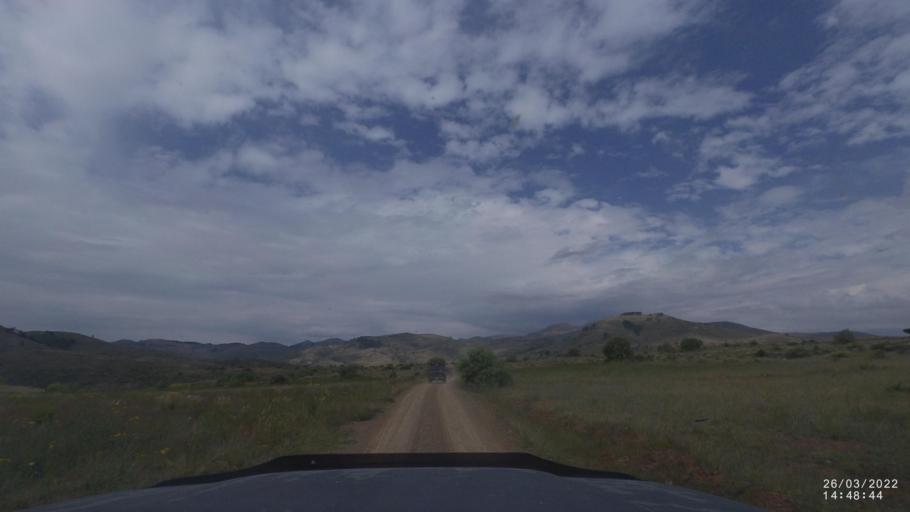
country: BO
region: Cochabamba
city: Cliza
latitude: -17.7261
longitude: -65.8559
